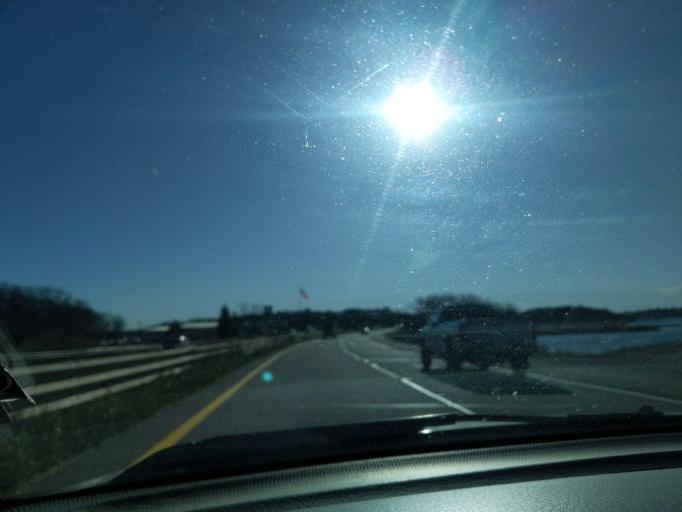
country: US
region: Massachusetts
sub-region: Essex County
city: Gloucester
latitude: 42.6257
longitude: -70.7053
